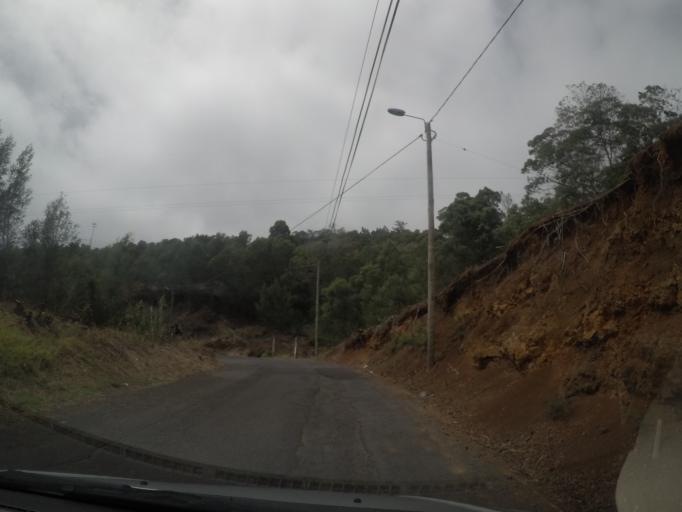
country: PT
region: Madeira
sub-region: Machico
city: Machico
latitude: 32.7026
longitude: -16.7885
